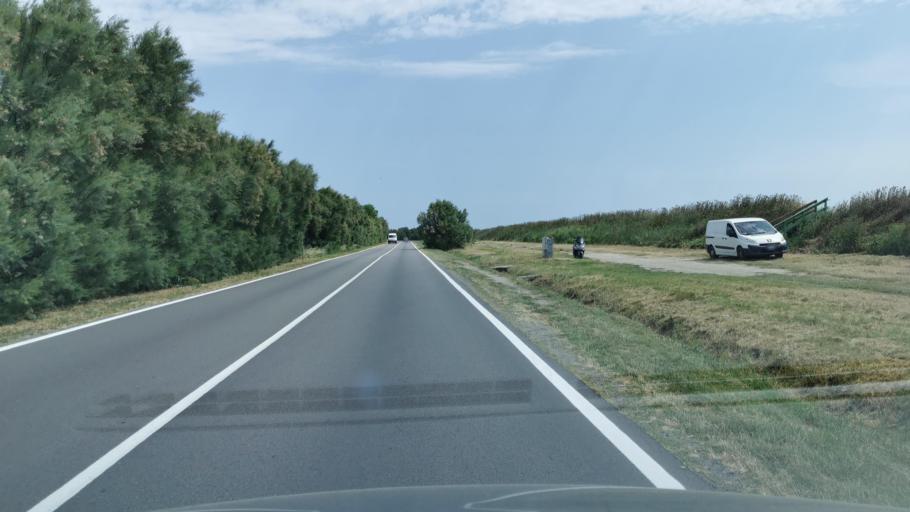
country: IT
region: Emilia-Romagna
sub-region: Provincia di Ferrara
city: Comacchio
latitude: 44.6834
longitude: 12.1975
